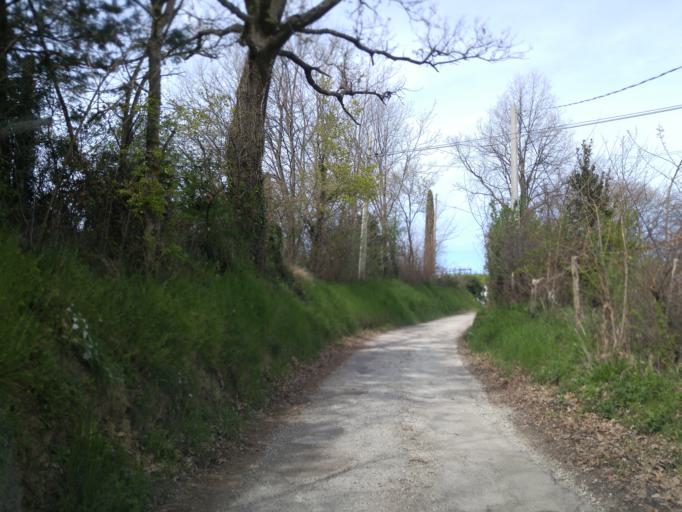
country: IT
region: The Marches
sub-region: Provincia di Pesaro e Urbino
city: Cartoceto
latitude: 43.7630
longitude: 12.8914
